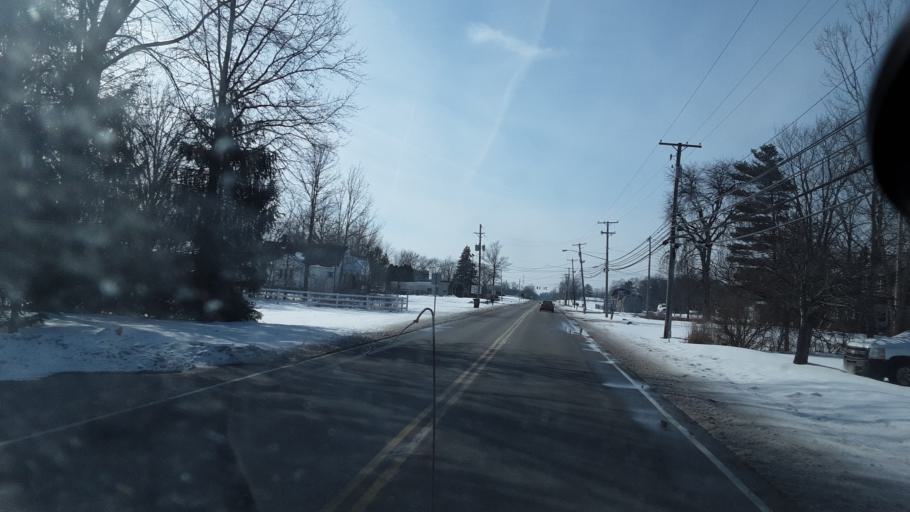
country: US
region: Ohio
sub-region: Mahoning County
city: Canfield
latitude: 41.0248
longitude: -80.7833
